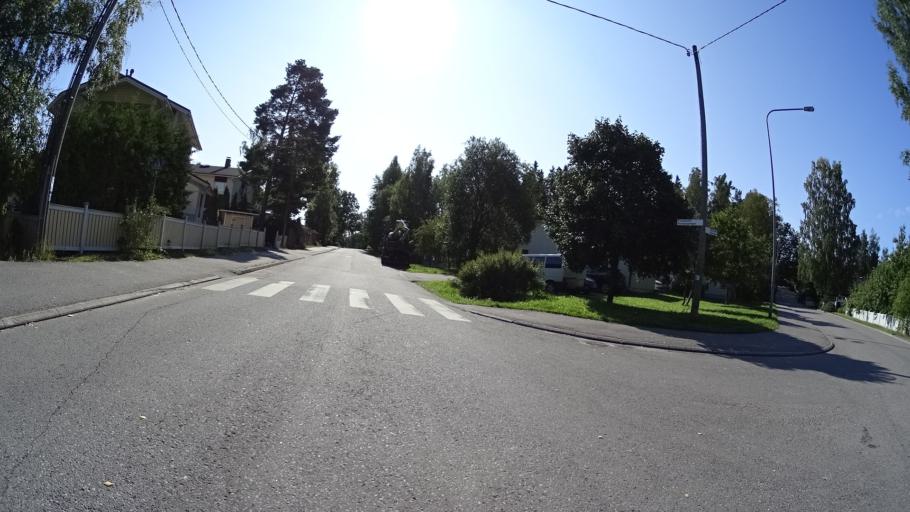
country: FI
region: Uusimaa
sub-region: Helsinki
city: Kauniainen
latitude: 60.2362
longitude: 24.6954
